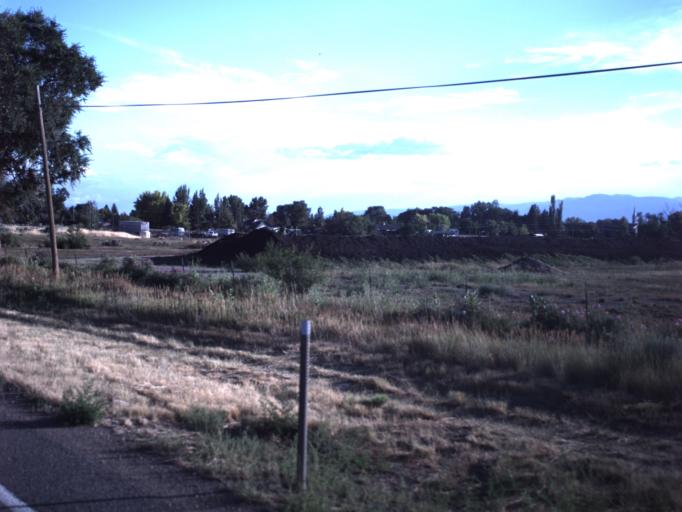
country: US
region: Utah
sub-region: Sanpete County
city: Mount Pleasant
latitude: 39.5573
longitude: -111.4555
